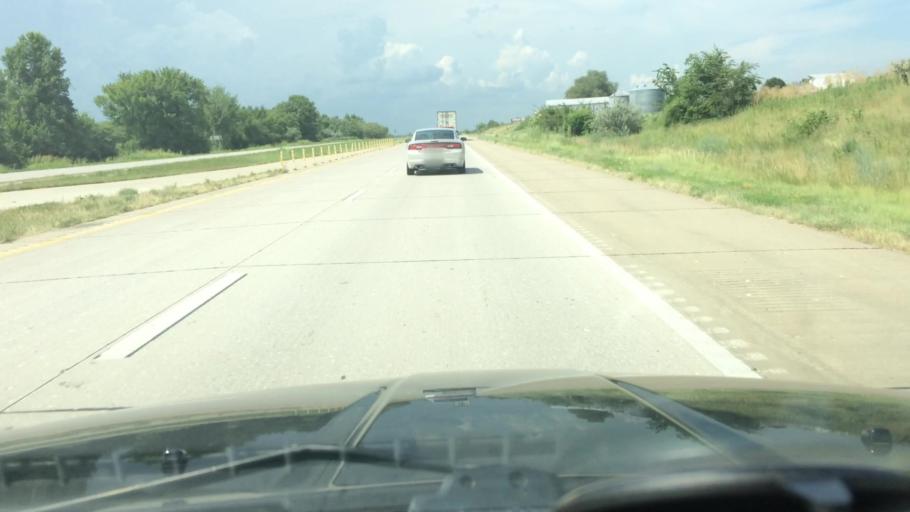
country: US
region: Missouri
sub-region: Henry County
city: Clinton
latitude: 38.3050
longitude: -93.7584
